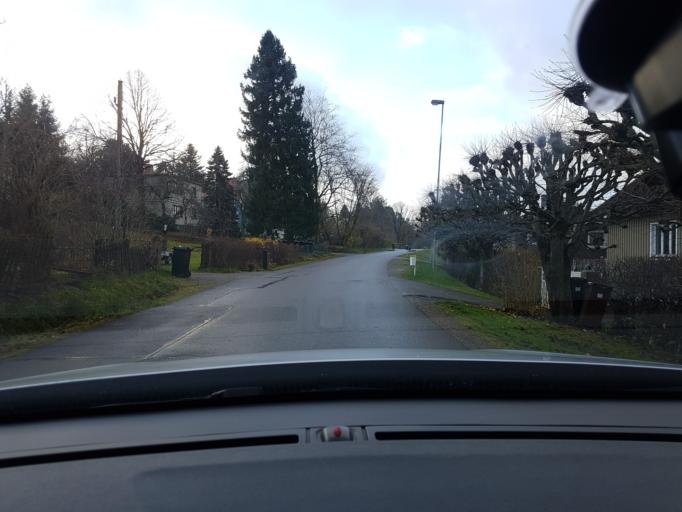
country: SE
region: Vaestra Goetaland
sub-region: Ale Kommun
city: Alafors
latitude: 57.9200
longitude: 12.0738
